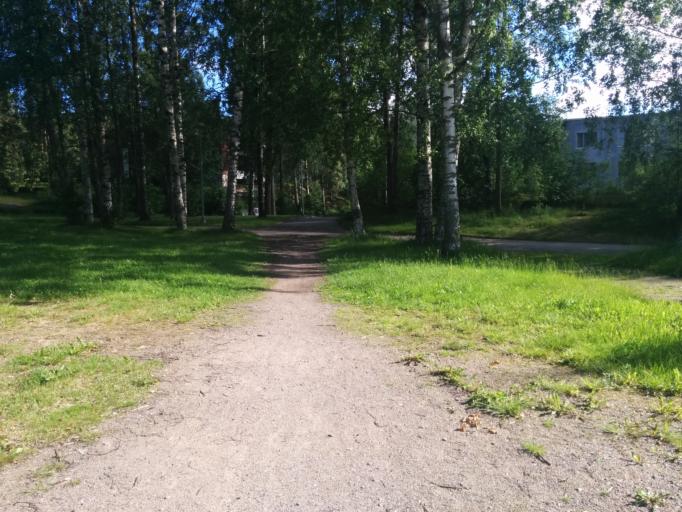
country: FI
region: Uusimaa
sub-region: Helsinki
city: Vantaa
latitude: 60.2443
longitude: 25.1123
